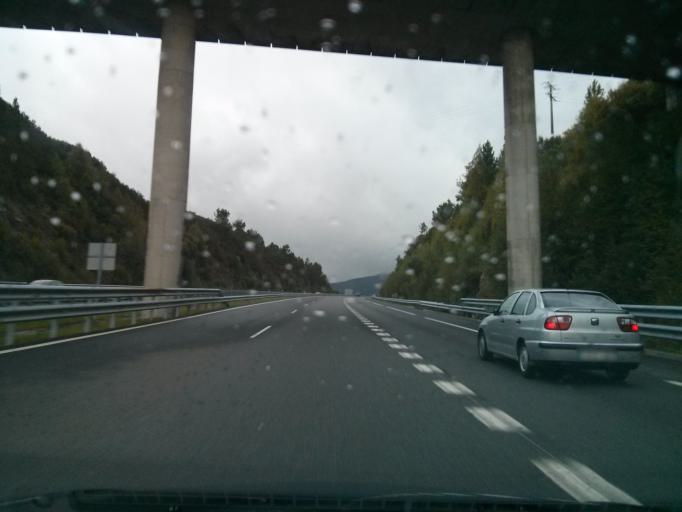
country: ES
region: Galicia
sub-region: Provincia de Ourense
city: Melon
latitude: 42.2837
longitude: -8.2027
